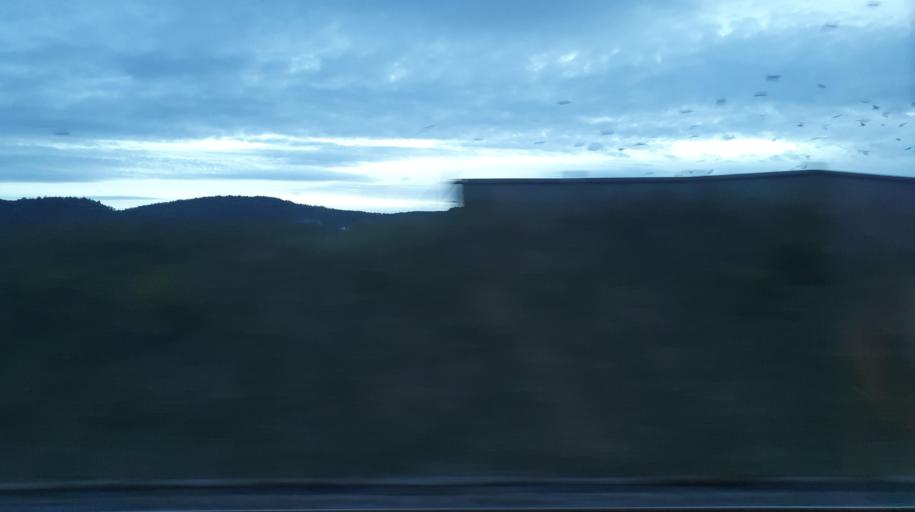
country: NO
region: Vestfold
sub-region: Sande
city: Sande
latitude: 59.5823
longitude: 10.2065
